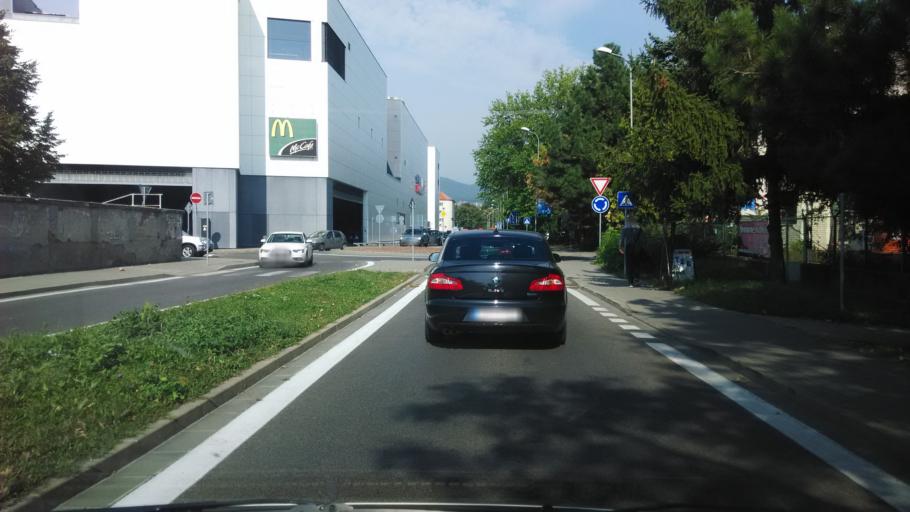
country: SK
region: Nitriansky
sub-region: Okres Nitra
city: Nitra
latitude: 48.3057
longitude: 18.0863
